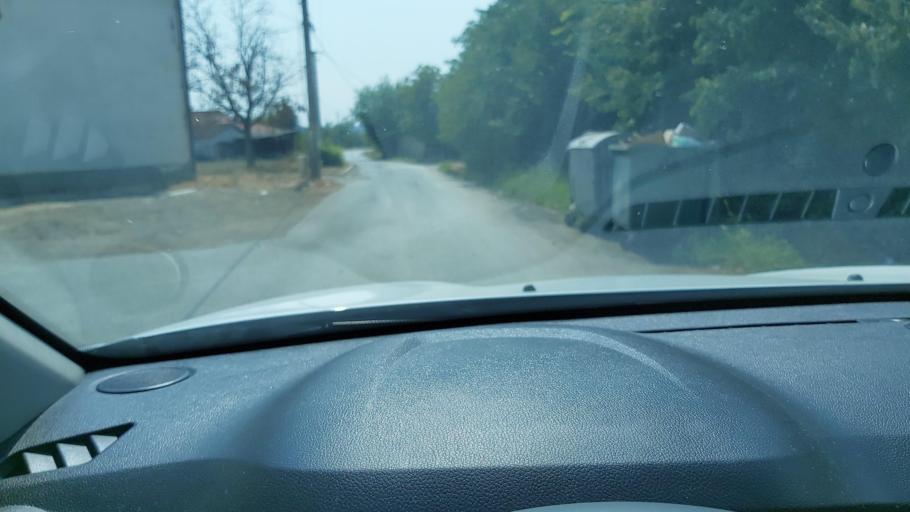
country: MK
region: Gevgelija
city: Gevgelija
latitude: 41.1647
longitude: 22.5047
